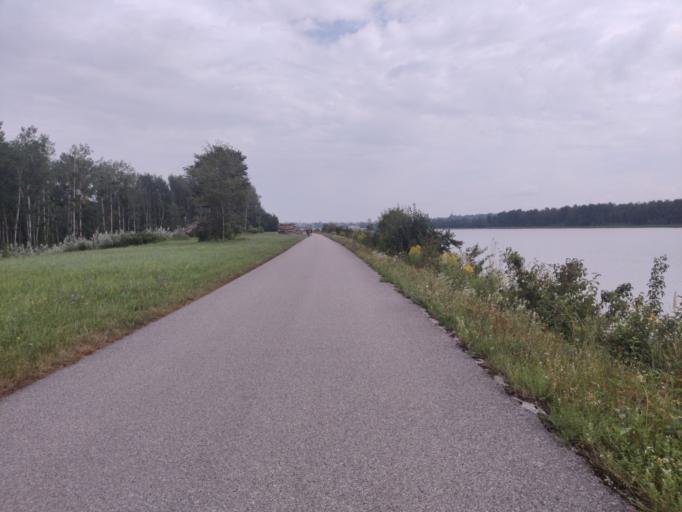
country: AT
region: Lower Austria
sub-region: Politischer Bezirk Amstetten
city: Strengberg
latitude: 48.1671
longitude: 14.6728
